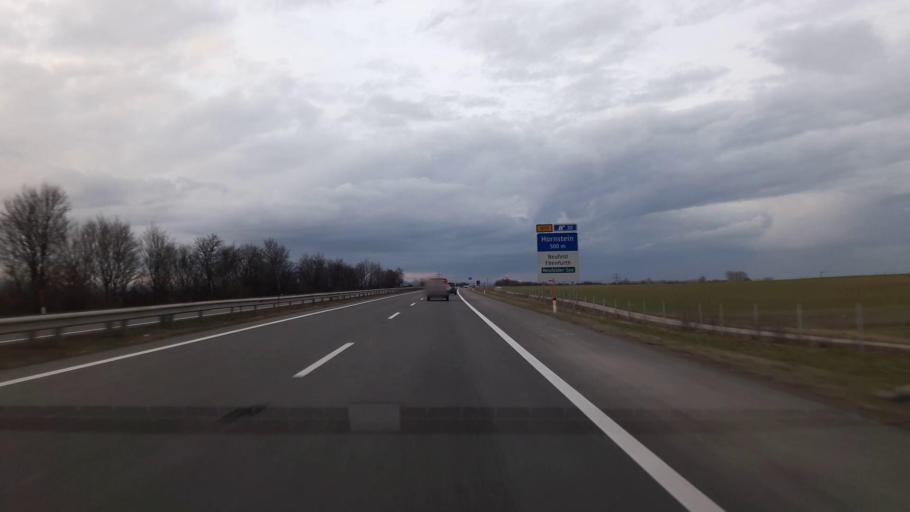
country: AT
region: Burgenland
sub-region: Eisenstadt-Umgebung
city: Steinbrunn
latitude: 47.8575
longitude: 16.4236
